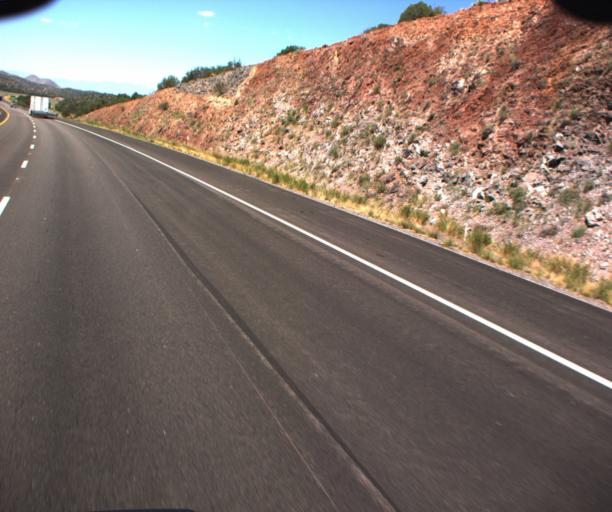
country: US
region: Arizona
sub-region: Mohave County
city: Peach Springs
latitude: 35.1904
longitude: -113.4412
